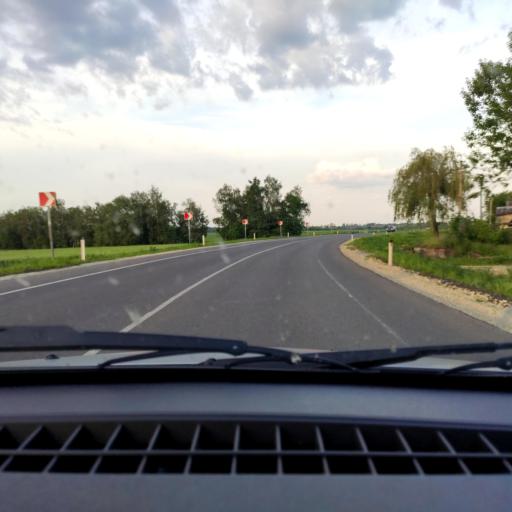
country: RU
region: Voronezj
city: Ramon'
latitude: 51.9228
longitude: 39.2960
